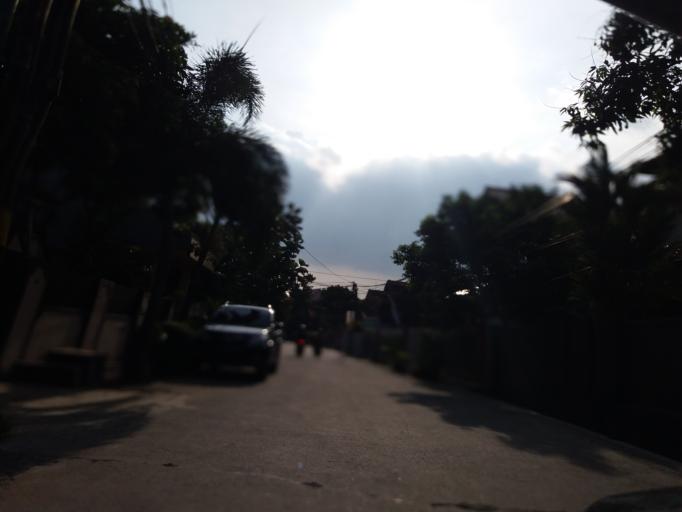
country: ID
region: West Java
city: Bandung
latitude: -6.9521
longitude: 107.6307
